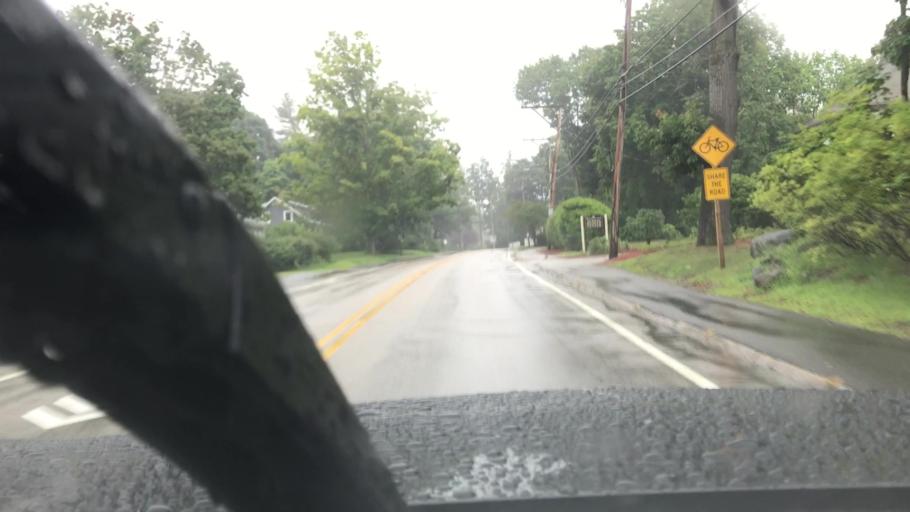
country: US
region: New Hampshire
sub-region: Strafford County
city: Durham
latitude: 43.1383
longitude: -70.9261
